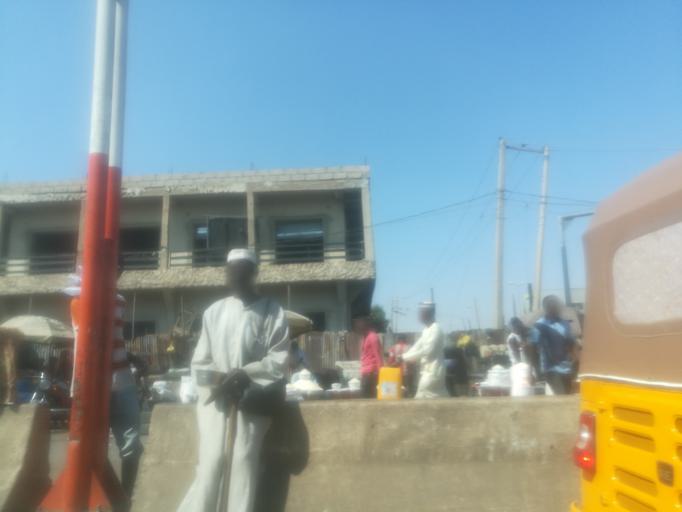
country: NG
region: Kano
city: Kano
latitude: 12.0141
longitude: 8.5346
